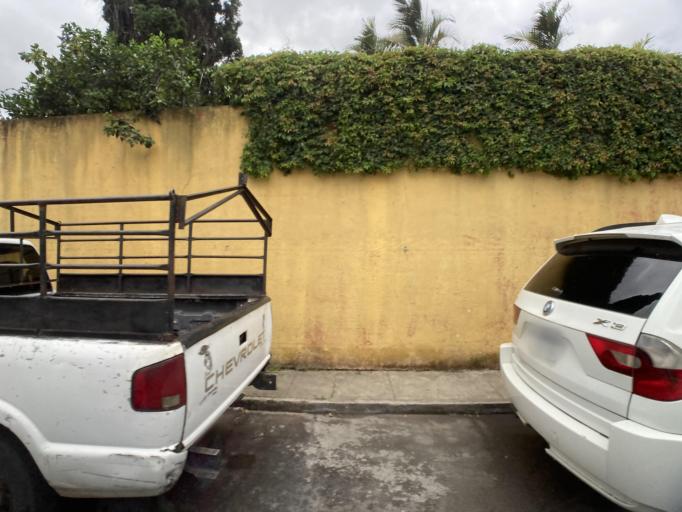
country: GT
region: Sacatepequez
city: Jocotenango
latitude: 14.5784
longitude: -90.7475
